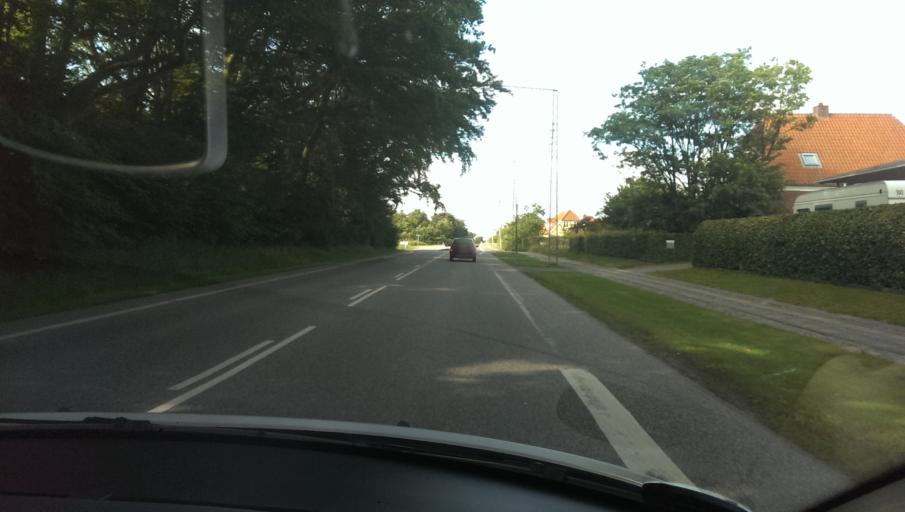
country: DK
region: Central Jutland
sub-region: Ringkobing-Skjern Kommune
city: Ringkobing
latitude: 56.1000
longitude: 8.2543
